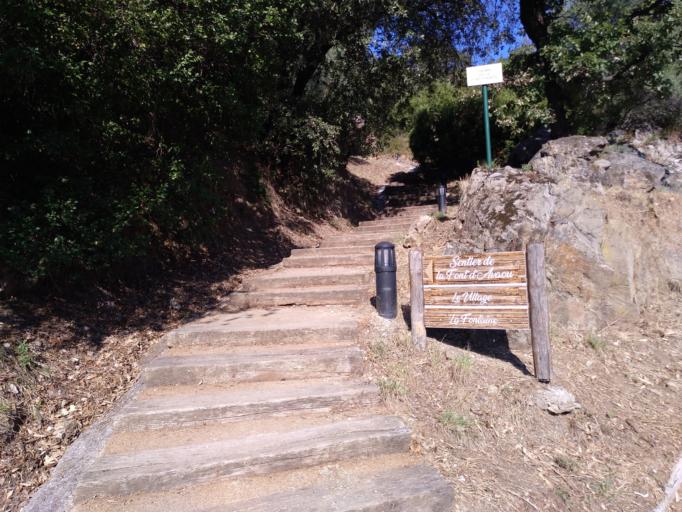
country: FR
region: Provence-Alpes-Cote d'Azur
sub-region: Departement du Var
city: Ramatuelle
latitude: 43.2168
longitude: 6.6133
